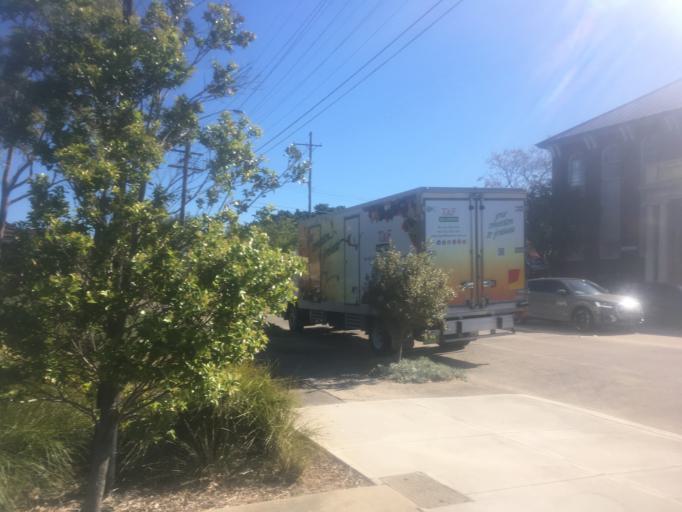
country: AU
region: New South Wales
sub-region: Marrickville
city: Newtown
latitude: -33.9156
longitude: 151.1679
